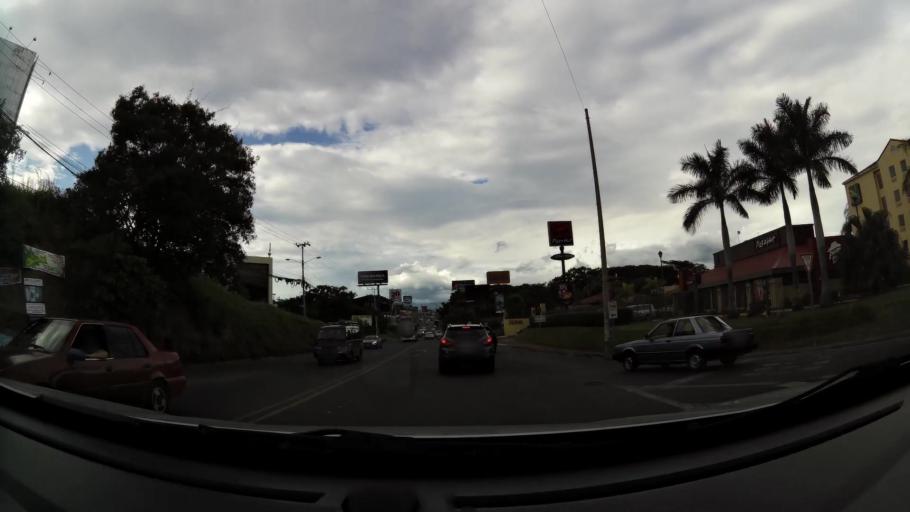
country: CR
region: San Jose
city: Santa Ana
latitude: 9.9449
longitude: -84.1909
